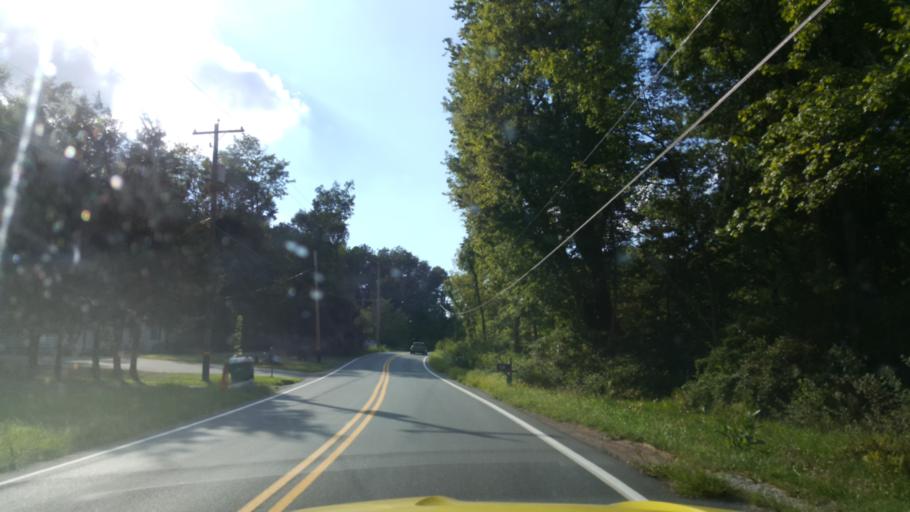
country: US
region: Pennsylvania
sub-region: Lebanon County
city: Campbelltown
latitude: 40.2506
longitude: -76.5434
